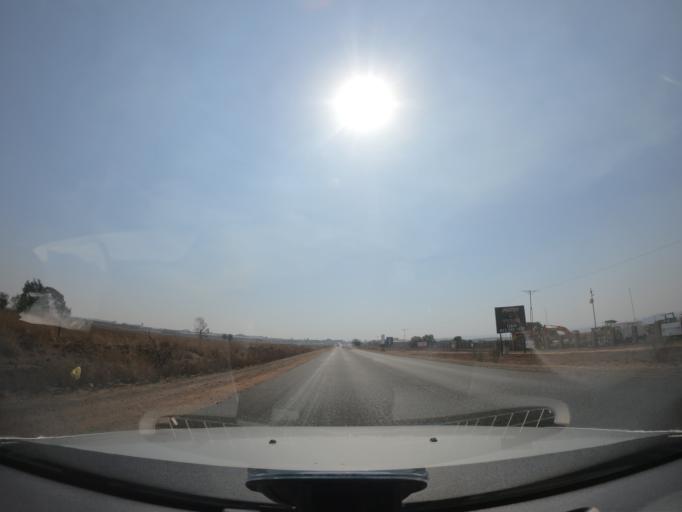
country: ZA
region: Mpumalanga
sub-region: Nkangala District Municipality
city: Middelburg
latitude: -25.8147
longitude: 29.4616
